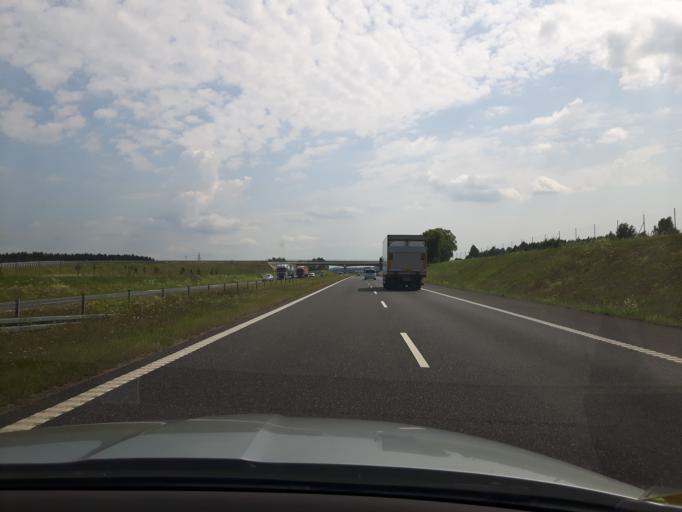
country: PL
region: Warmian-Masurian Voivodeship
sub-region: Powiat olsztynski
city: Olsztynek
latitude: 53.5175
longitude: 20.2925
